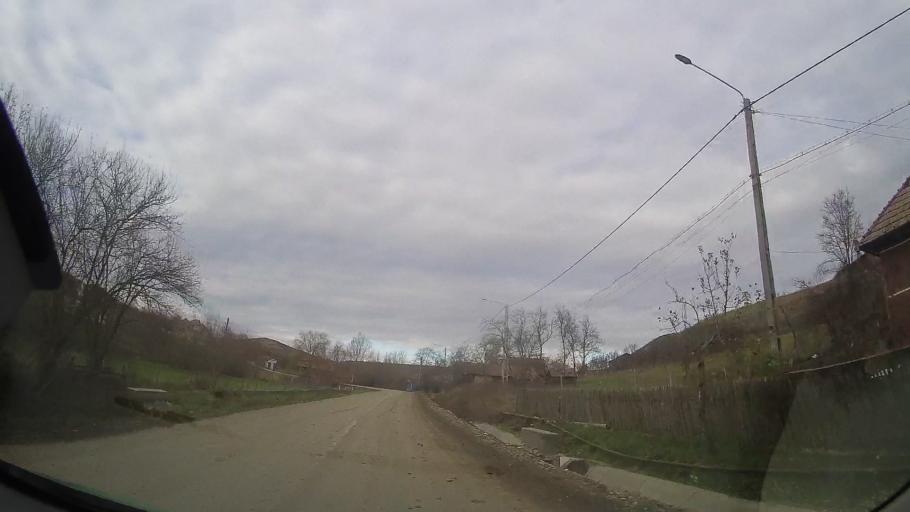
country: RO
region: Bistrita-Nasaud
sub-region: Comuna Micestii de Campie
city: Micestii de Campie
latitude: 46.8312
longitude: 24.3064
